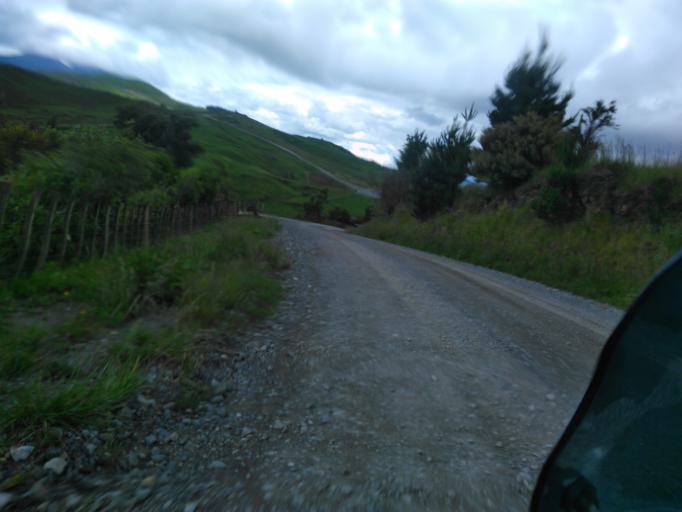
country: NZ
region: Gisborne
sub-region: Gisborne District
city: Gisborne
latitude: -38.0497
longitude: 178.0531
